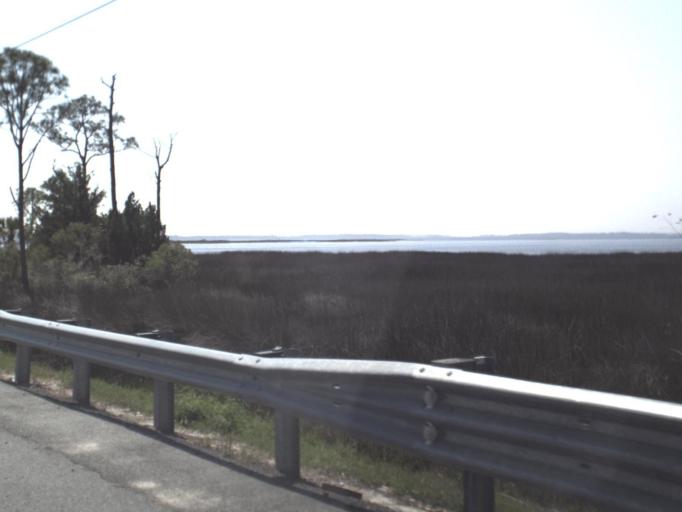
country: US
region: Florida
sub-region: Gulf County
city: Port Saint Joe
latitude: 29.7217
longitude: -85.3036
